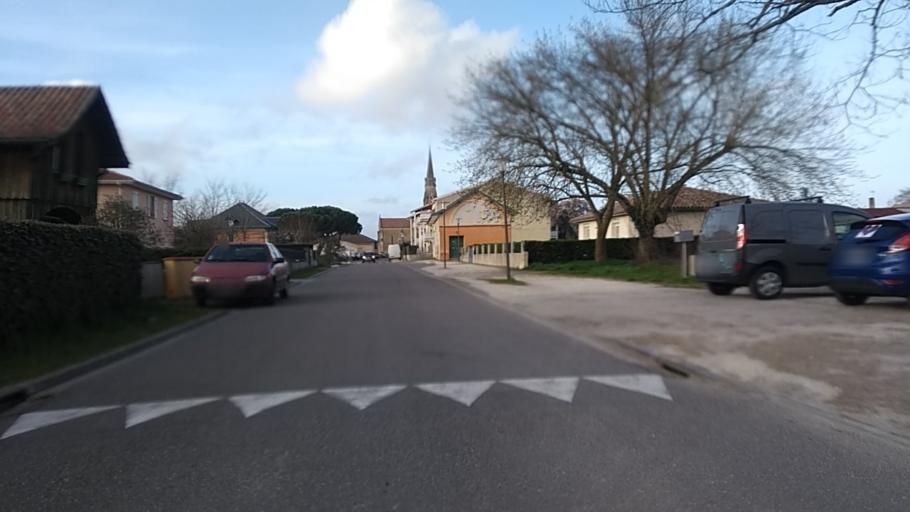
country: FR
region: Aquitaine
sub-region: Departement de la Gironde
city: Le Barp
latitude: 44.6042
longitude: -0.7691
